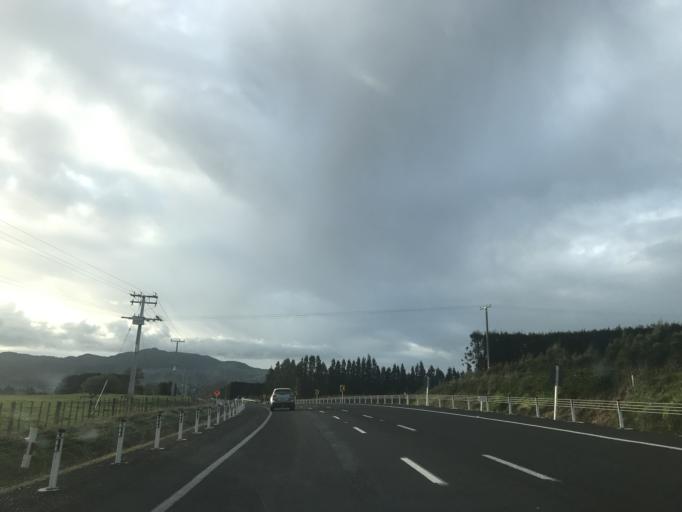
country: NZ
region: Waikato
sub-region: Hauraki District
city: Waihi
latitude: -37.4123
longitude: 175.8635
